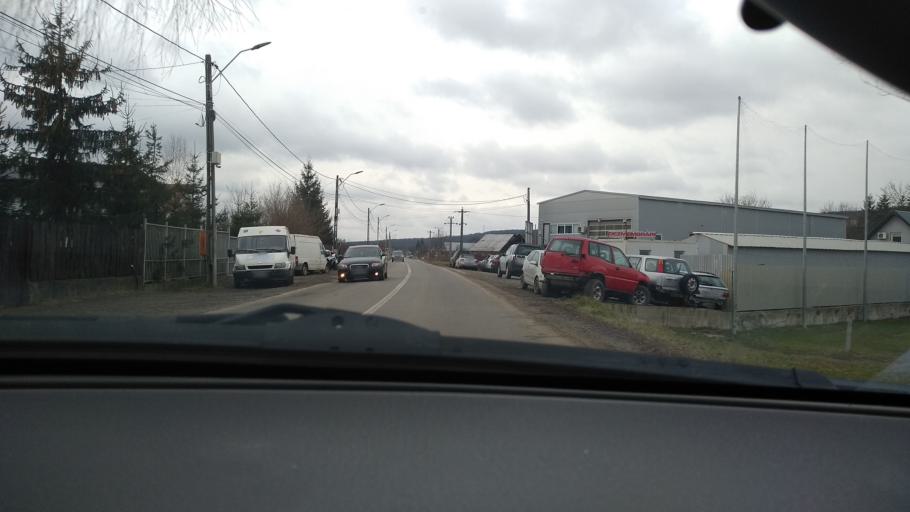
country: RO
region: Mures
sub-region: Comuna Livezeni
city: Livezeni
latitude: 46.5472
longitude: 24.6339
